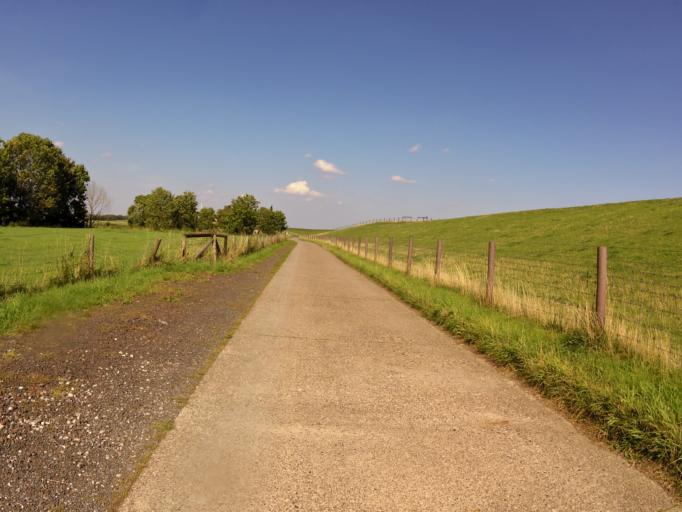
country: DE
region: Lower Saxony
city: Nordenham
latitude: 53.4113
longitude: 8.4701
